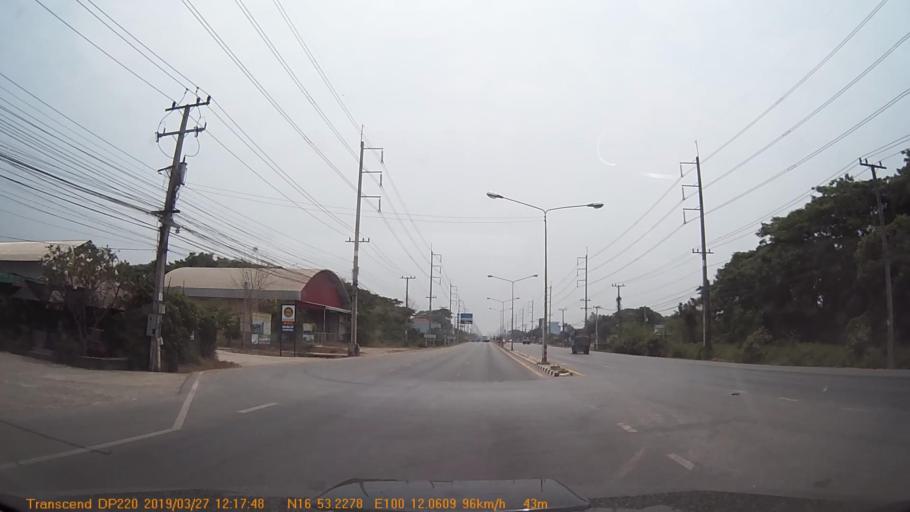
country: TH
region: Phitsanulok
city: Phitsanulok
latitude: 16.8867
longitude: 100.2012
